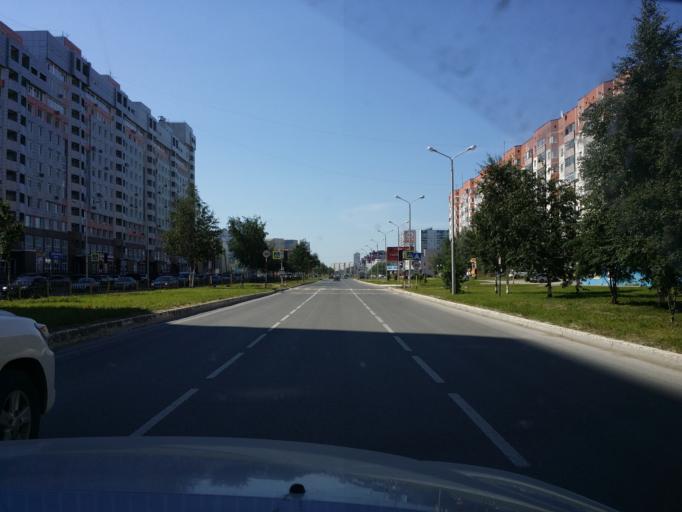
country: RU
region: Khanty-Mansiyskiy Avtonomnyy Okrug
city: Nizhnevartovsk
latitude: 60.9332
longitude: 76.5963
